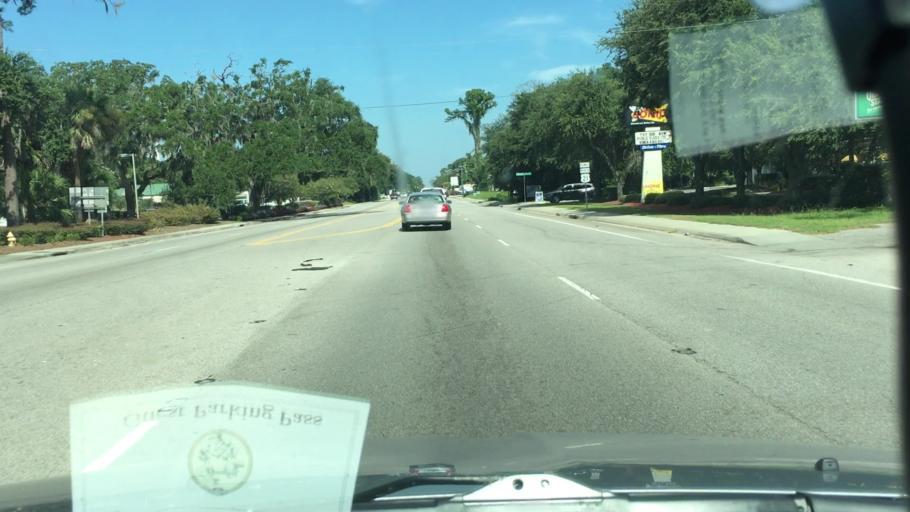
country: US
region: South Carolina
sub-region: Beaufort County
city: Beaufort
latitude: 32.4145
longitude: -80.6515
